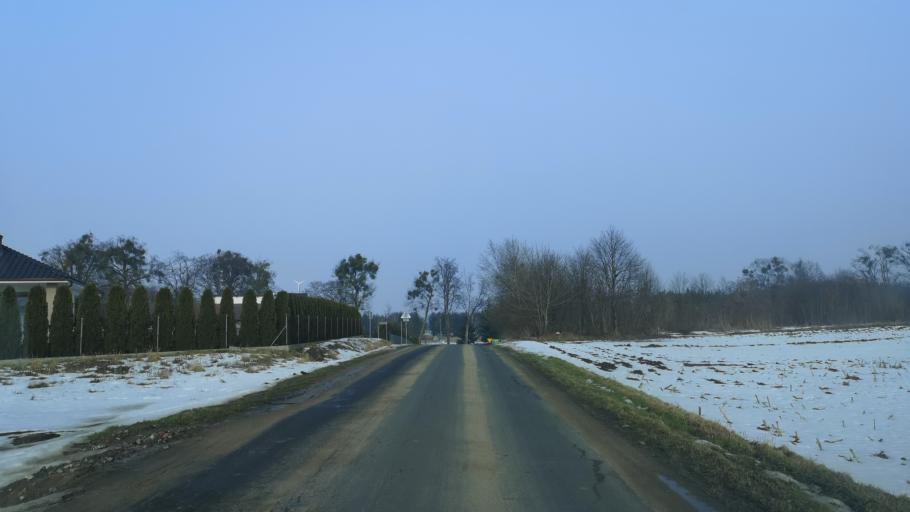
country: PL
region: Warmian-Masurian Voivodeship
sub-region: Powiat nowomiejski
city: Biskupiec
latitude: 53.4992
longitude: 19.3289
